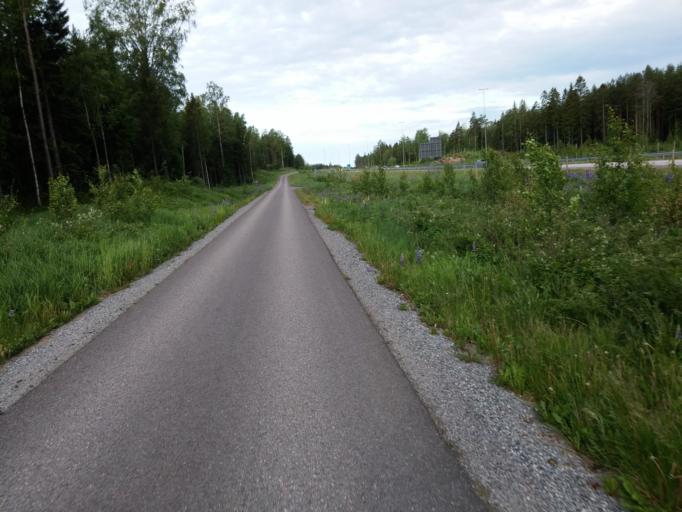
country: FI
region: Uusimaa
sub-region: Helsinki
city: Espoo
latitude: 60.1436
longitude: 24.5623
